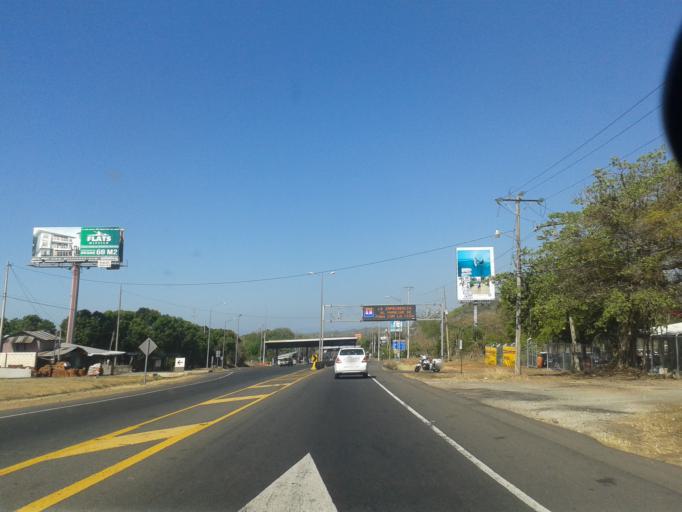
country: CR
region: Alajuela
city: Orotina
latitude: 9.8889
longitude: -84.5678
